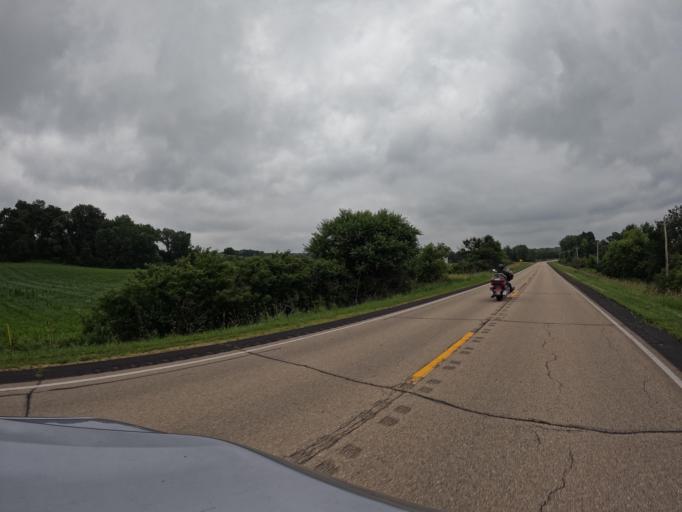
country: US
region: Illinois
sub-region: Carroll County
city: Savanna
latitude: 42.0021
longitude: -90.1843
